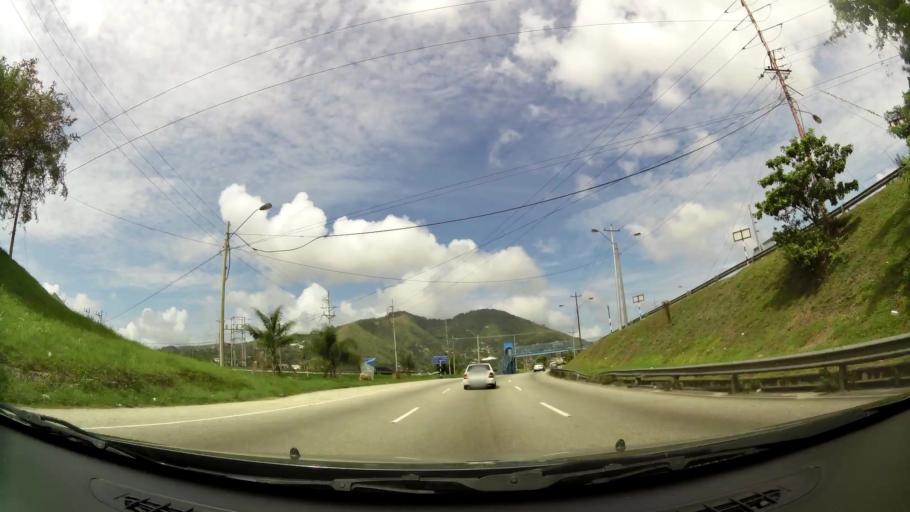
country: TT
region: City of Port of Spain
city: Mucurapo
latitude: 10.6795
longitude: -61.5523
